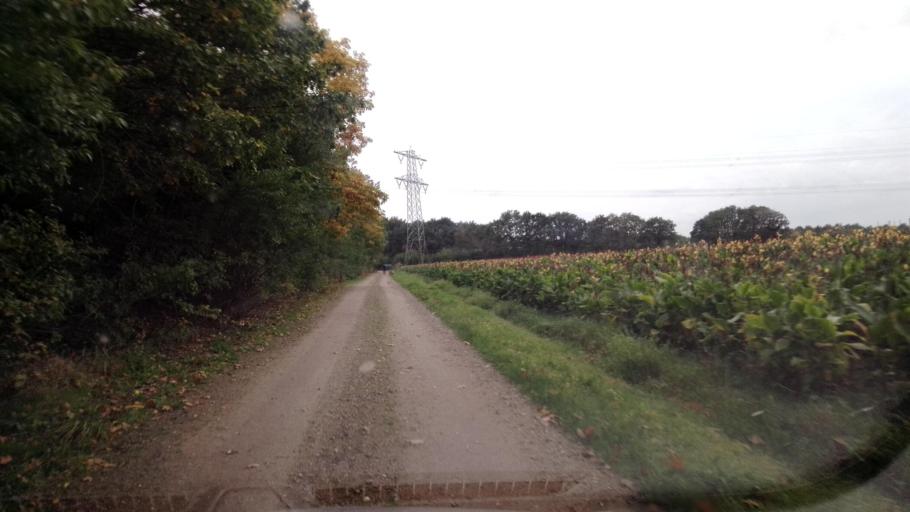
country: NL
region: Limburg
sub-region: Gemeente Venlo
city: Tegelen
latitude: 51.3952
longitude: 6.1140
